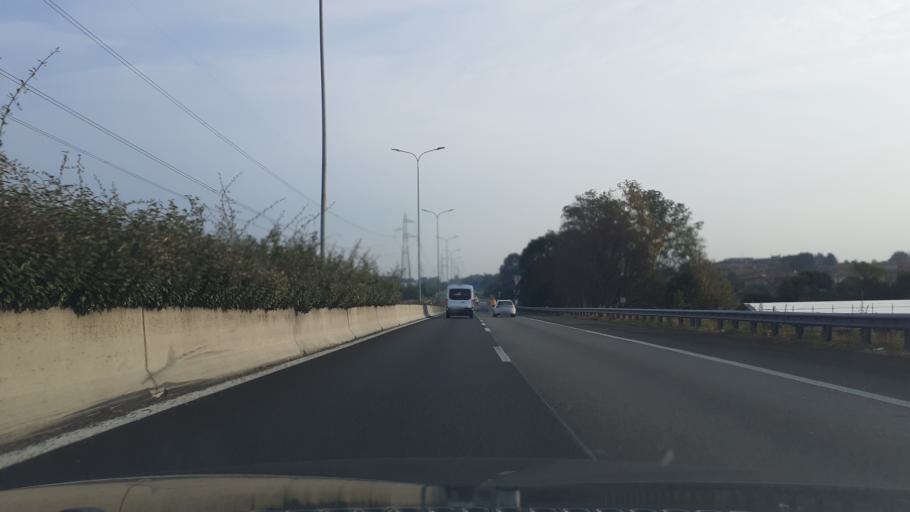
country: IT
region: Lombardy
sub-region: Provincia di Monza e Brianza
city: Verano Brianza
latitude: 45.6867
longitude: 9.2170
